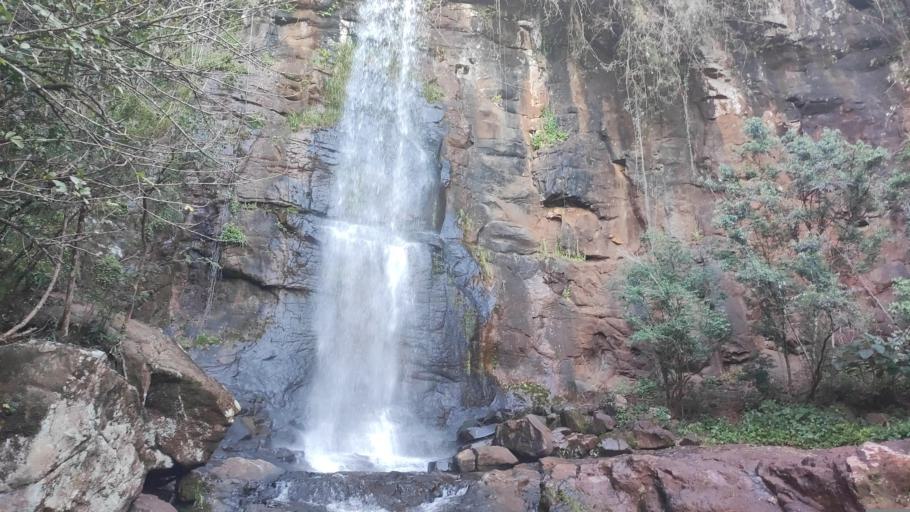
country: AR
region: Misiones
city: Dos de Mayo
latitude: -26.9940
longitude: -54.6337
